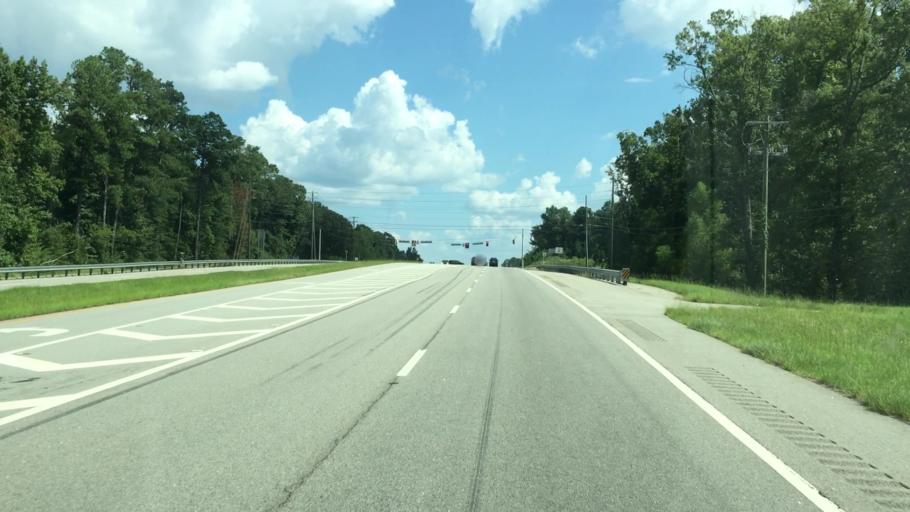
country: US
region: Georgia
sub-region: Putnam County
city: Eatonton
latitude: 33.2389
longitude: -83.3205
